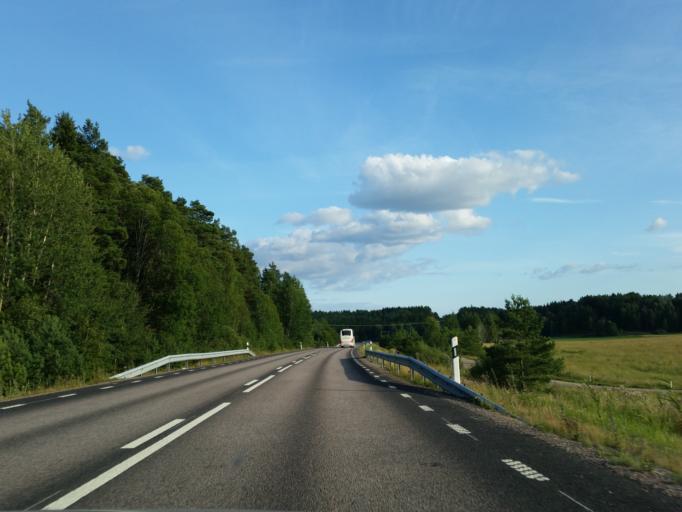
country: SE
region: Soedermanland
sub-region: Gnesta Kommun
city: Gnesta
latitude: 59.0430
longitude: 17.2921
